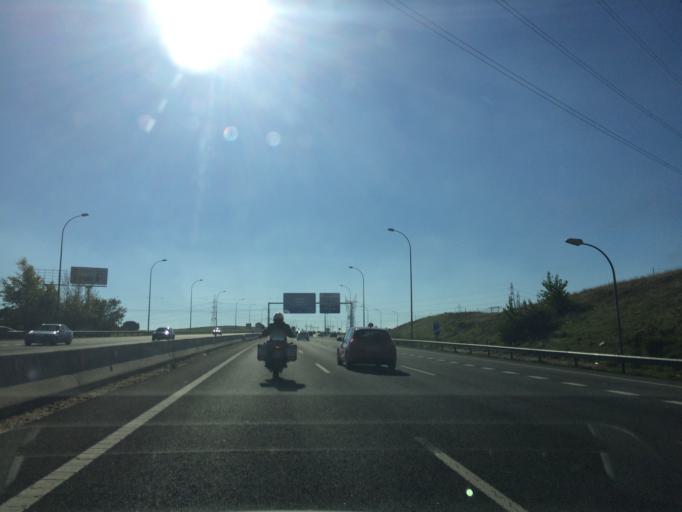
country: ES
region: Madrid
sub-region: Provincia de Madrid
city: San Sebastian de los Reyes
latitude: 40.5698
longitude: -3.5881
